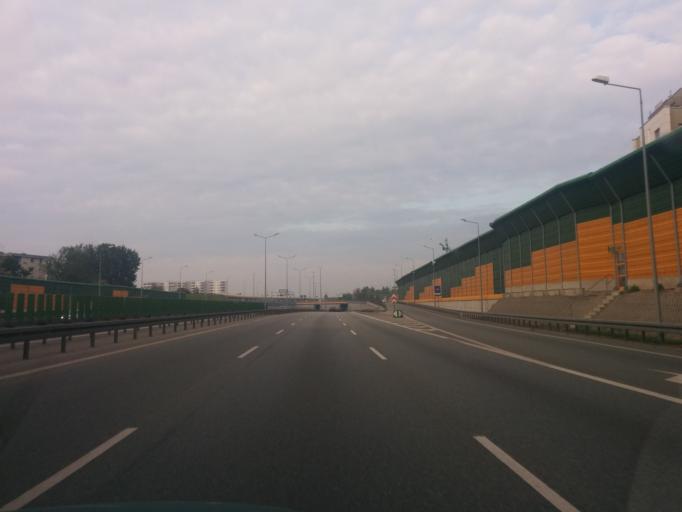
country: PL
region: Masovian Voivodeship
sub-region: Warszawa
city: Bemowo
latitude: 52.2452
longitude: 20.9036
